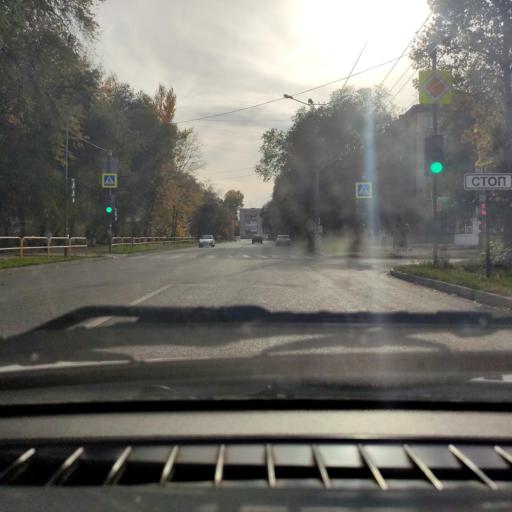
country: RU
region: Samara
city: Tol'yatti
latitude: 53.5233
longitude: 49.4278
